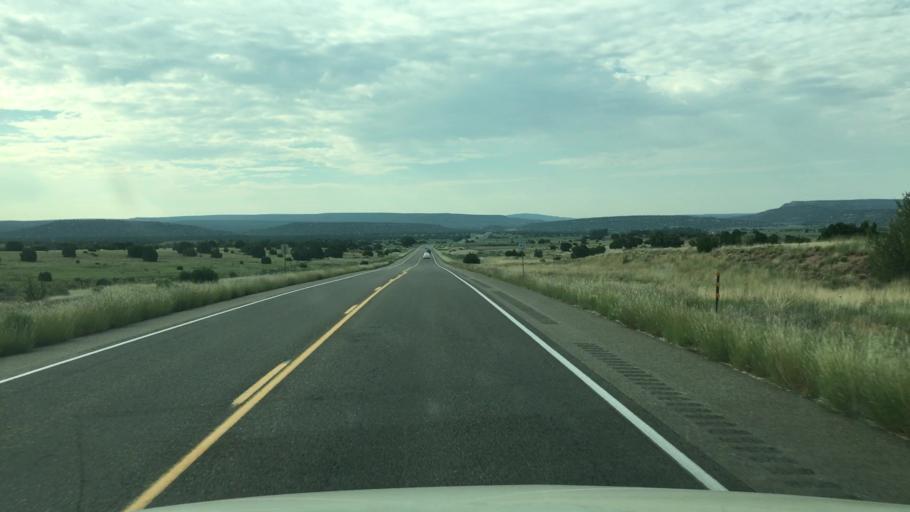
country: US
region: New Mexico
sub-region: Santa Fe County
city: Eldorado at Santa Fe
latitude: 35.4190
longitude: -105.8718
